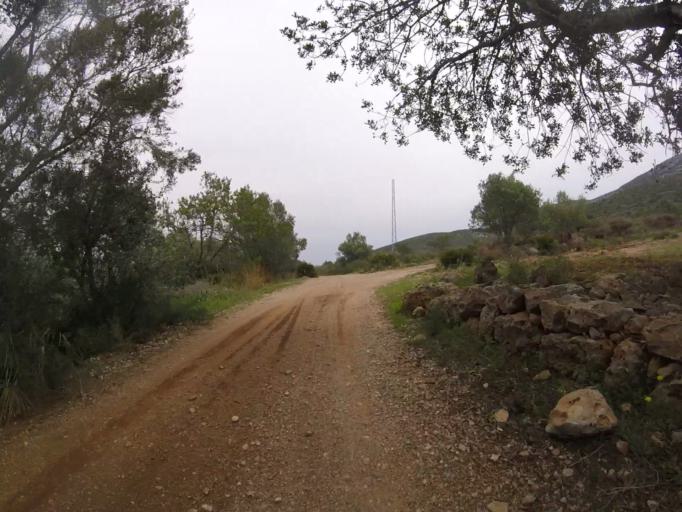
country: ES
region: Valencia
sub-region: Provincia de Castello
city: Santa Magdalena de Pulpis
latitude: 40.3679
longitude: 0.3300
